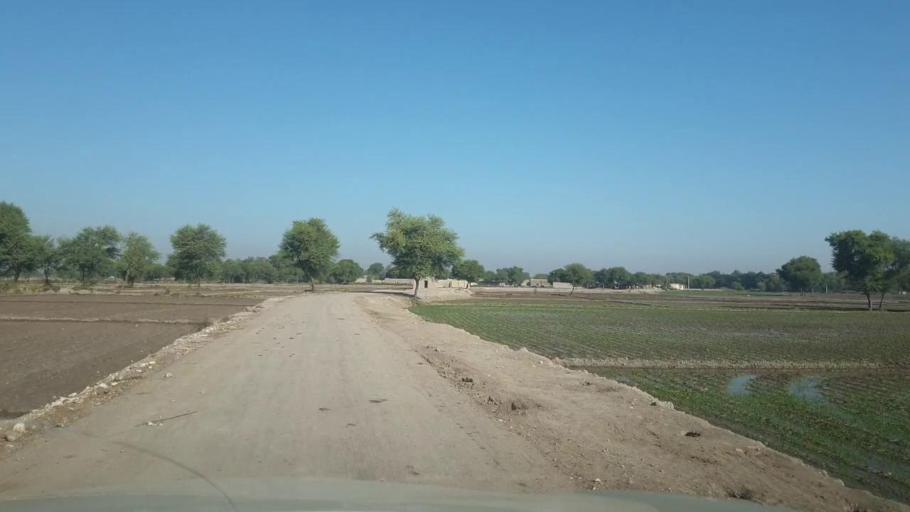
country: PK
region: Sindh
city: Bhan
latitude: 26.5409
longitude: 67.6727
